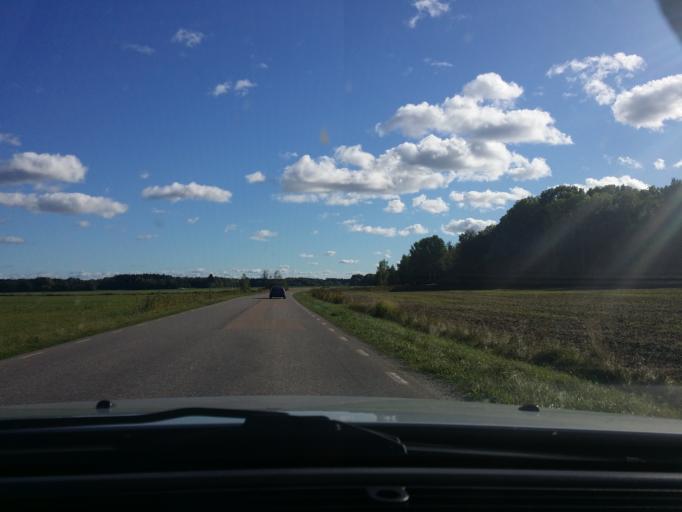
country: SE
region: Vaestmanland
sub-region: Vasteras
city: Vasteras
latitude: 59.5832
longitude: 16.4928
